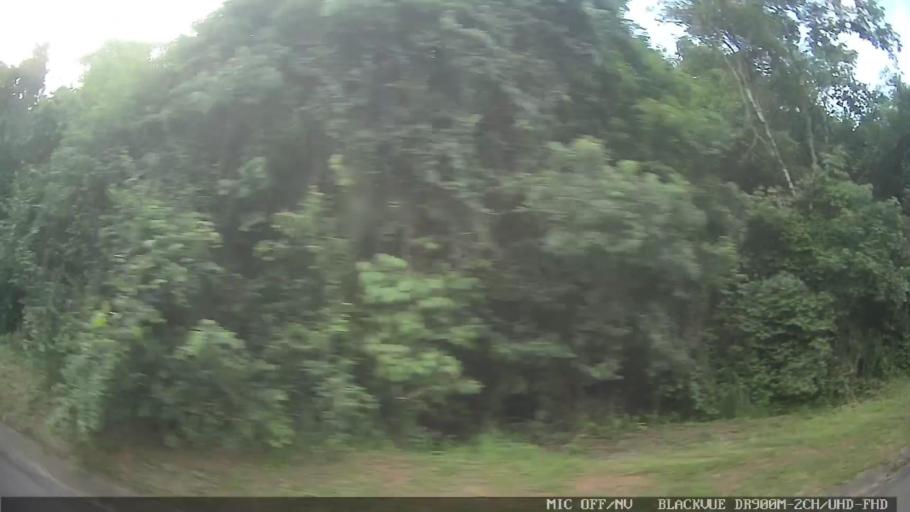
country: BR
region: Sao Paulo
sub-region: Porto Feliz
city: Porto Feliz
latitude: -23.2189
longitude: -47.5716
